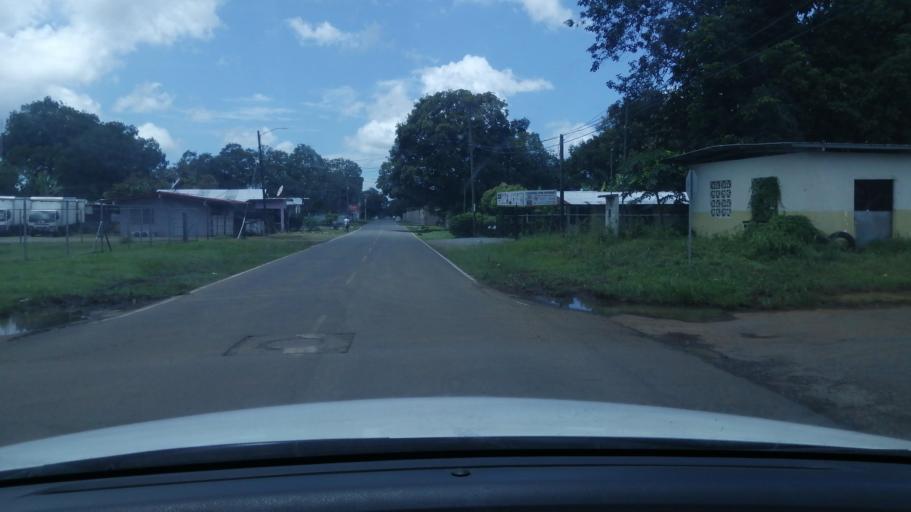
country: PA
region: Chiriqui
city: David
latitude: 8.4402
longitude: -82.4254
